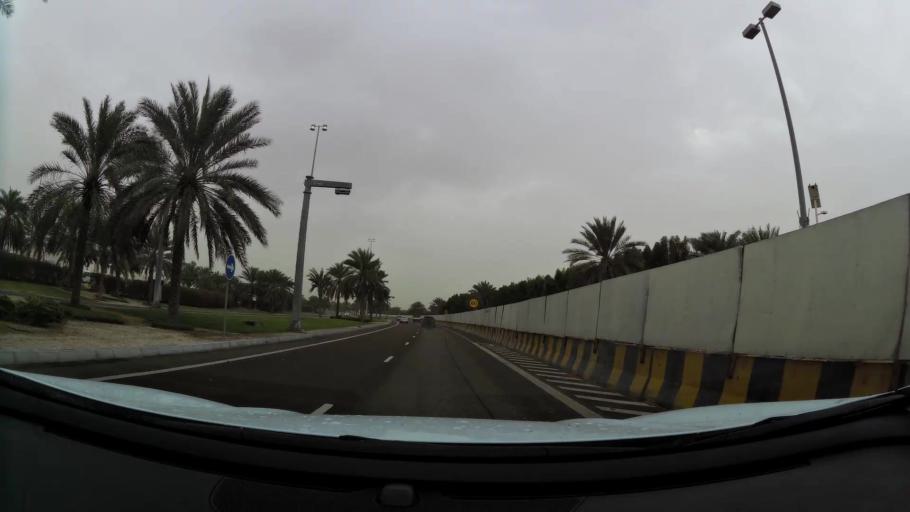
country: AE
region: Abu Dhabi
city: Abu Dhabi
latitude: 24.4379
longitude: 54.6228
